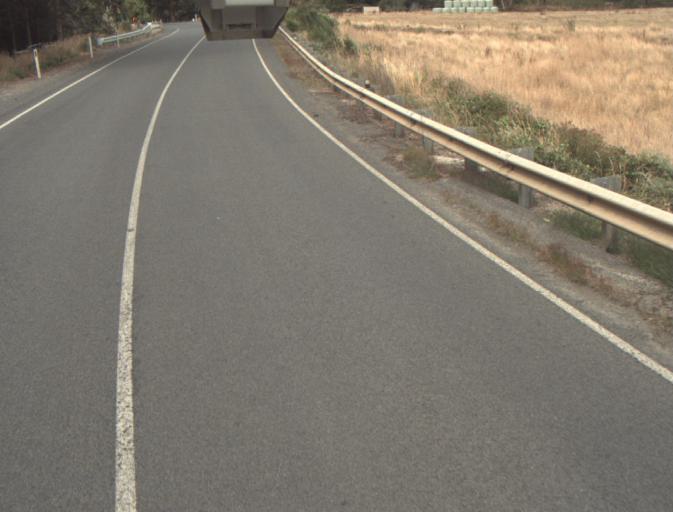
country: AU
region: Tasmania
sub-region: Launceston
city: Mayfield
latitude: -41.2281
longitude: 147.2090
